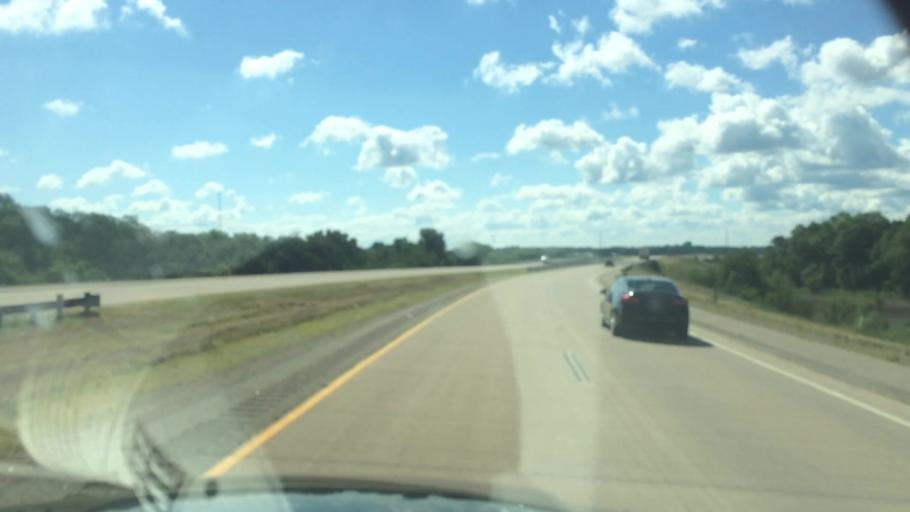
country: US
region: Wisconsin
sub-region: Portage County
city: Amherst
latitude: 44.4736
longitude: -89.3240
